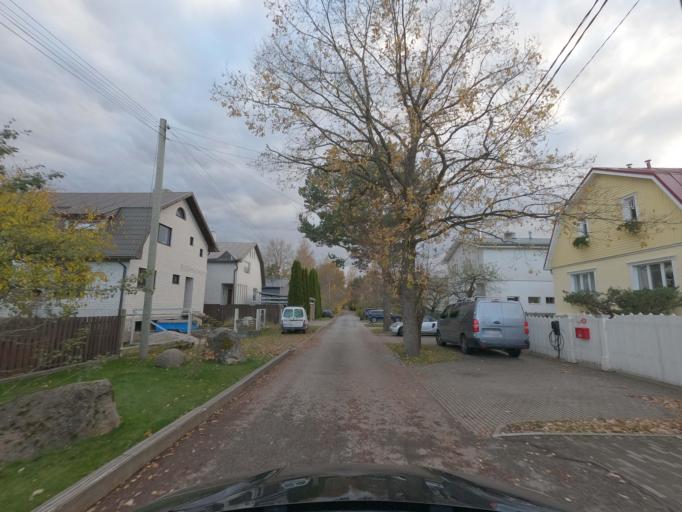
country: EE
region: Harju
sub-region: Saue linn
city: Saue
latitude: 59.3152
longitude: 24.5429
